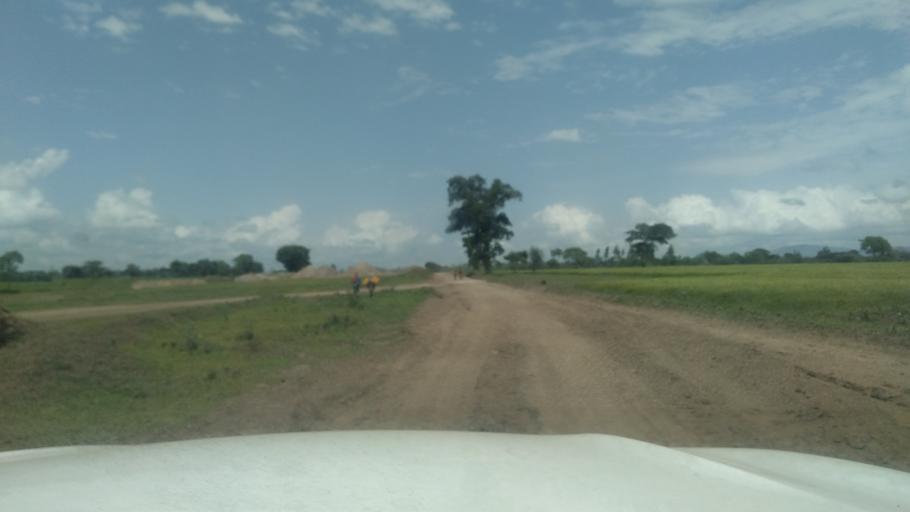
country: ET
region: Oromiya
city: Shashemene
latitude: 7.2747
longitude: 38.6015
